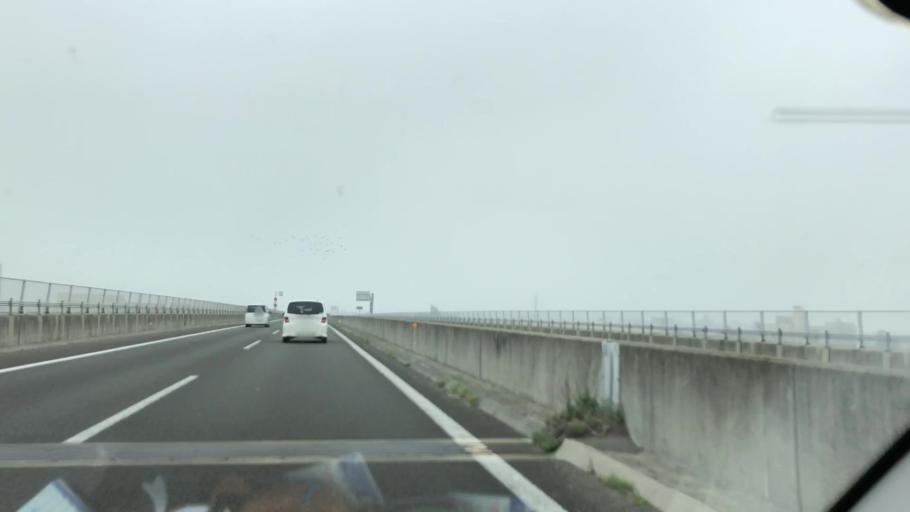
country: JP
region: Miyagi
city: Rifu
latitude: 38.2653
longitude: 140.9729
